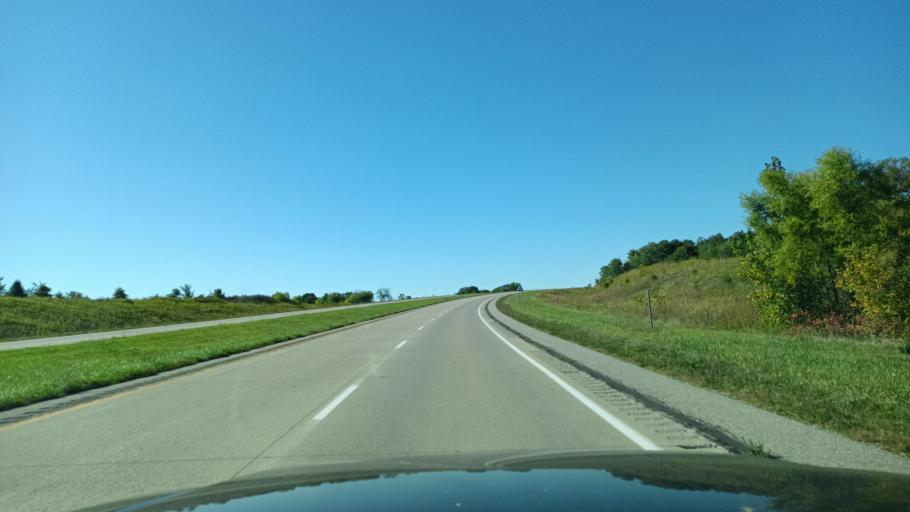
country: US
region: Iowa
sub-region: Lee County
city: Fort Madison
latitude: 40.6561
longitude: -91.3615
